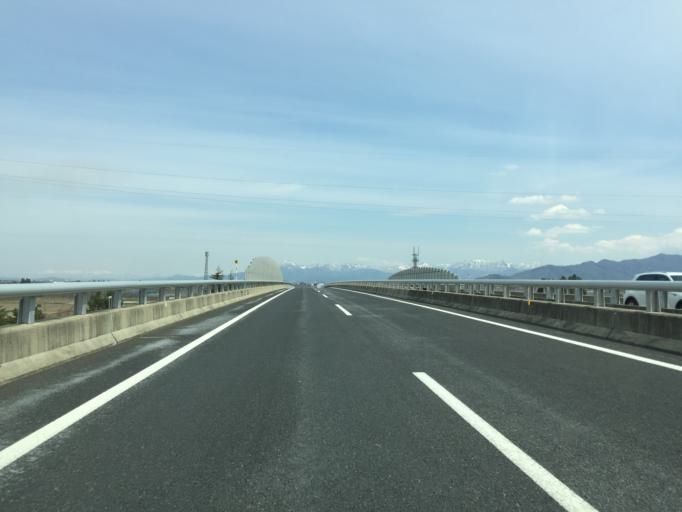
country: JP
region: Yamagata
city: Tendo
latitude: 38.3098
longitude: 140.3170
